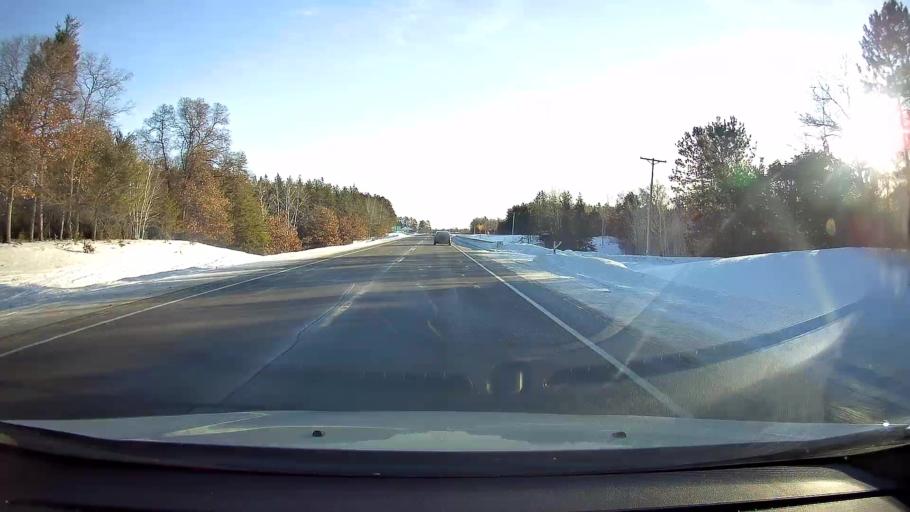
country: US
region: Wisconsin
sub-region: Washburn County
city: Spooner
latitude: 45.9104
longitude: -91.7729
